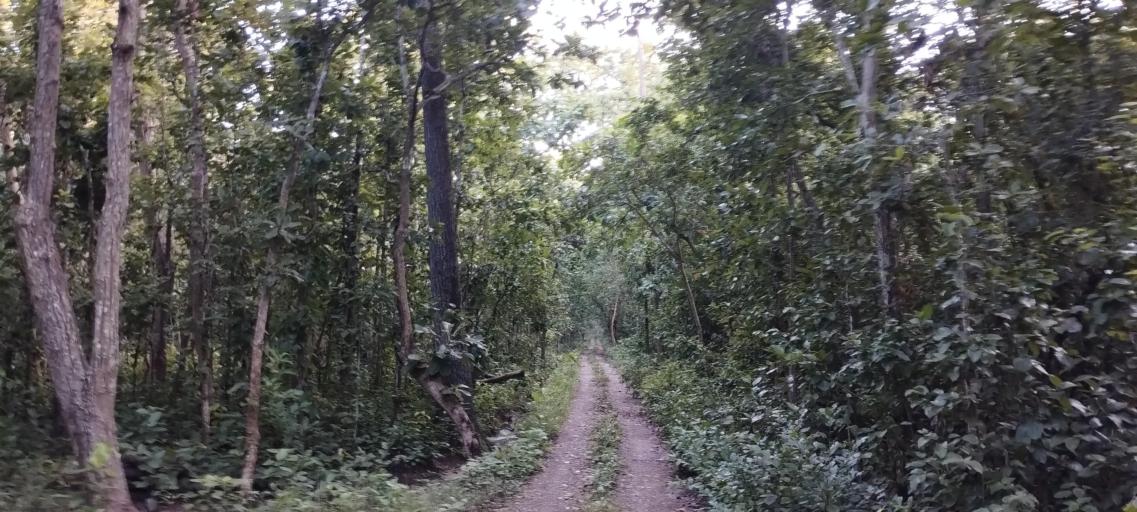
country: NP
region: Far Western
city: Tikapur
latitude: 28.4823
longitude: 81.2611
